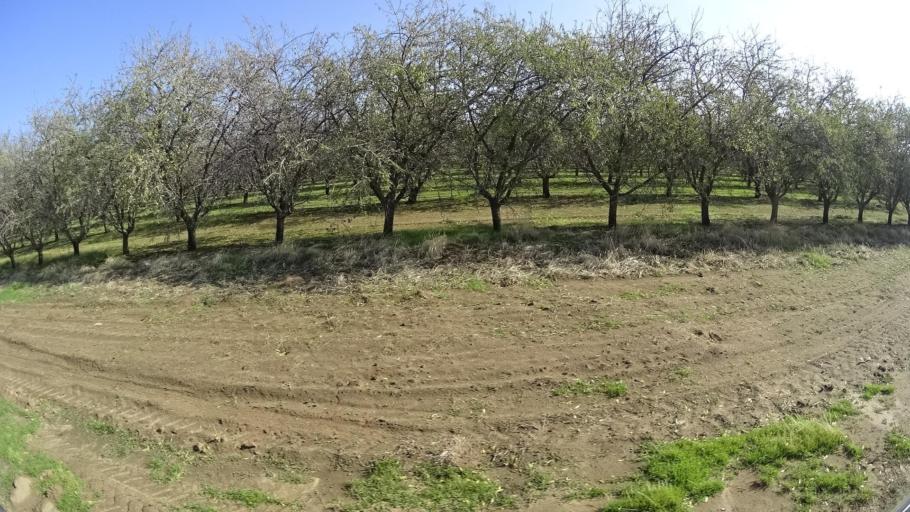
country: US
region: California
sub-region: Kern County
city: Arvin
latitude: 35.2665
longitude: -118.8070
